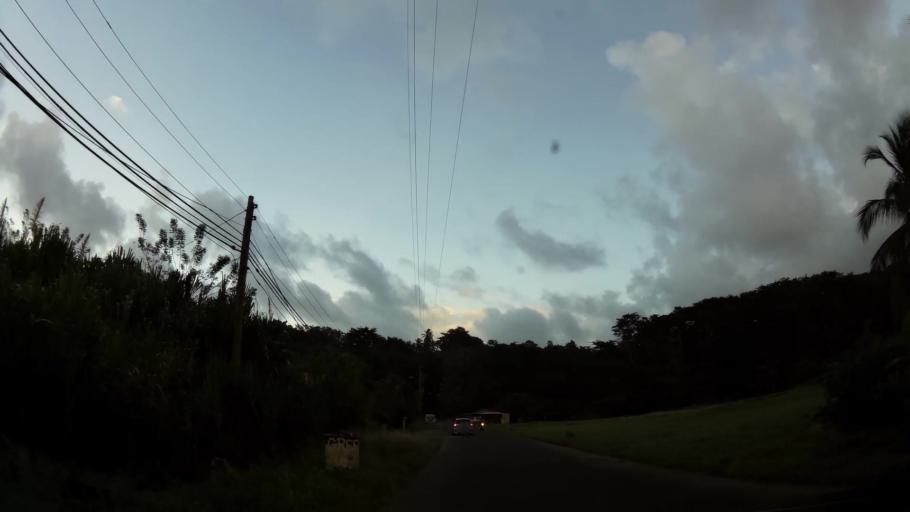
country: DM
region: Saint Andrew
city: Calibishie
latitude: 15.5929
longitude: -61.3792
